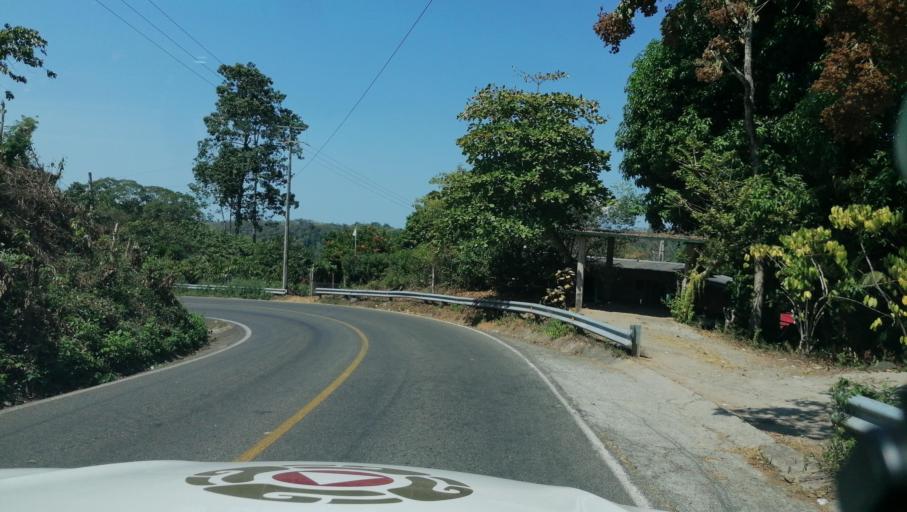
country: MX
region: Chiapas
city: Veinte de Noviembre
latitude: 14.9942
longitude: -92.2350
